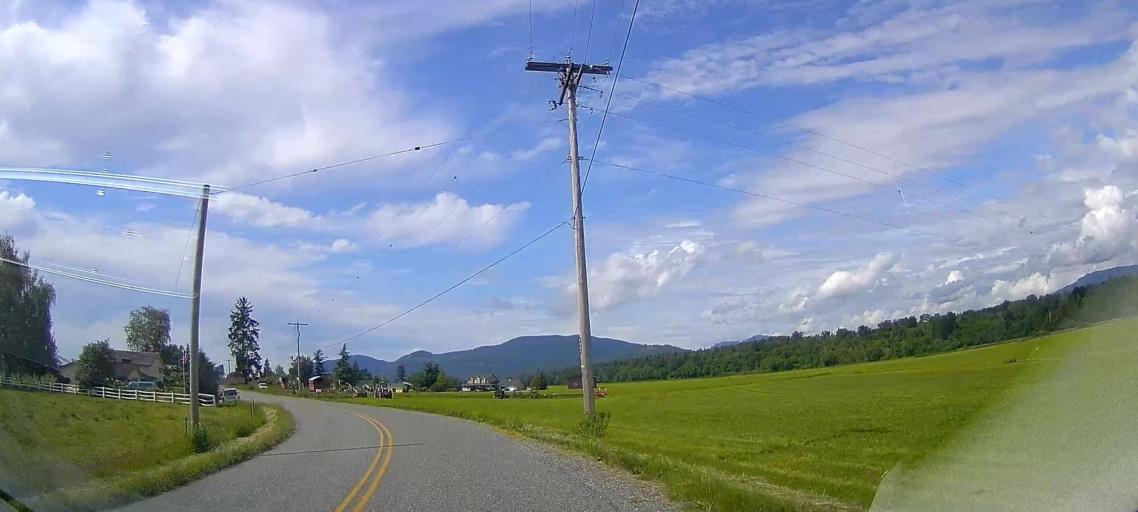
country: US
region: Washington
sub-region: Skagit County
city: Burlington
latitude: 48.5389
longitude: -122.3887
